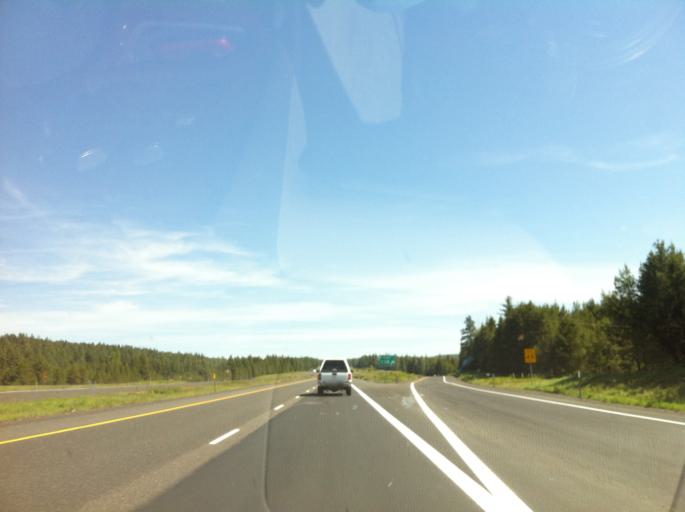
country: US
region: Oregon
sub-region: Umatilla County
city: Mission
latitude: 45.5123
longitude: -118.4315
